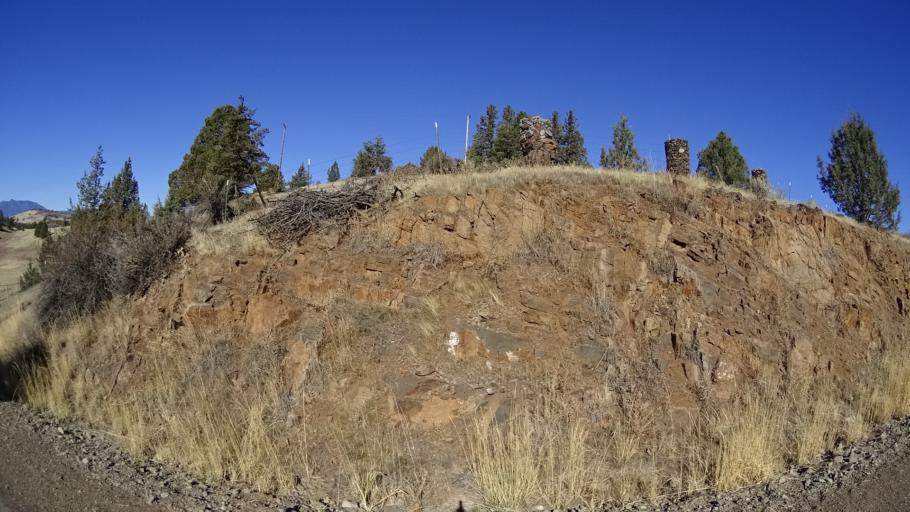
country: US
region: California
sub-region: Siskiyou County
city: Montague
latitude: 41.9229
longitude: -122.3683
